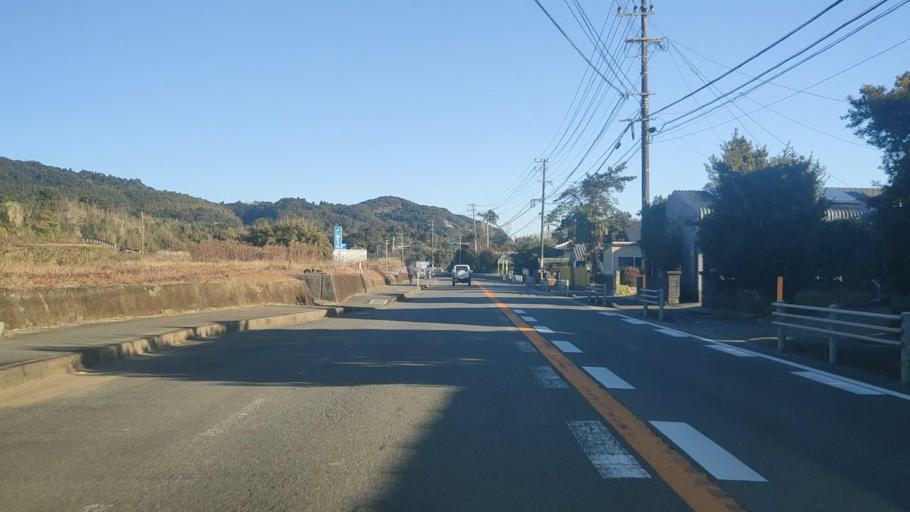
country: JP
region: Miyazaki
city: Nobeoka
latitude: 32.3611
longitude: 131.6223
